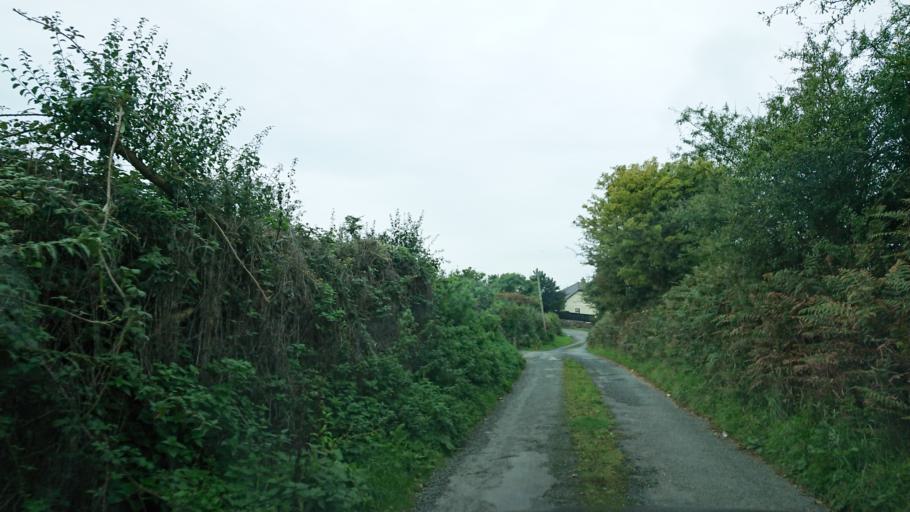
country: IE
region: Munster
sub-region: Waterford
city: Dunmore East
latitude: 52.1701
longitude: -6.9968
